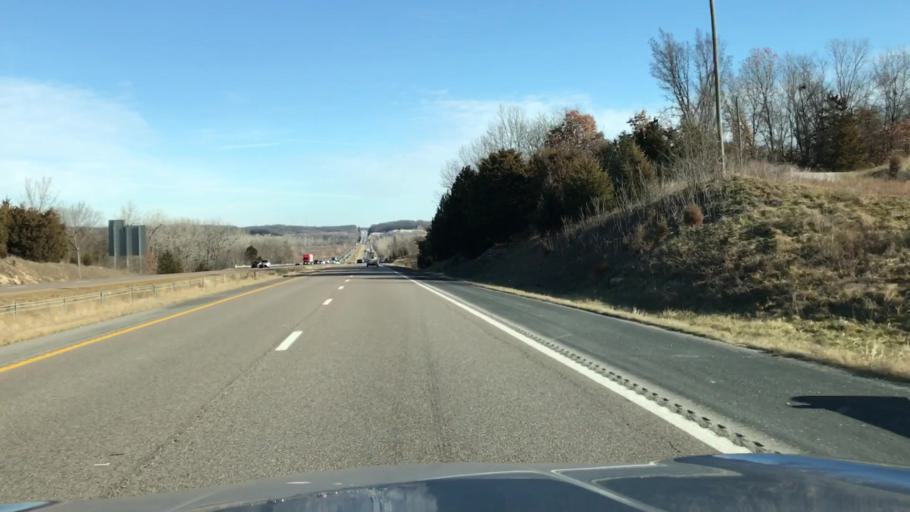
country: US
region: Missouri
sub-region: Cooper County
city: Boonville
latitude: 38.9419
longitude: -92.5727
